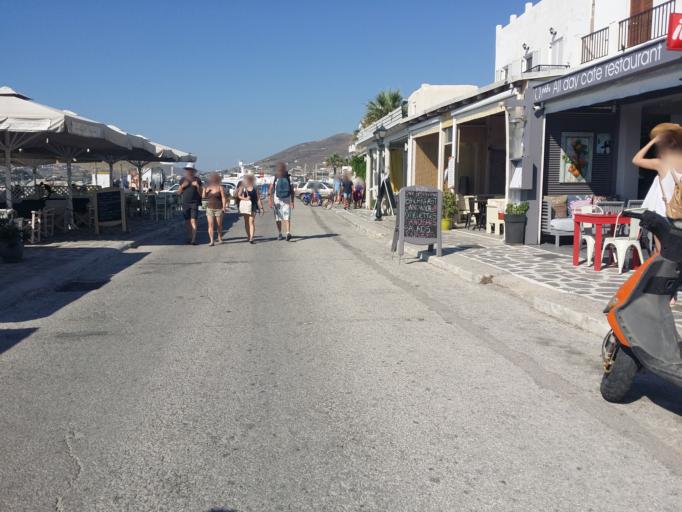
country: GR
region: South Aegean
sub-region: Nomos Kykladon
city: Paros
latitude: 37.0853
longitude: 25.1474
